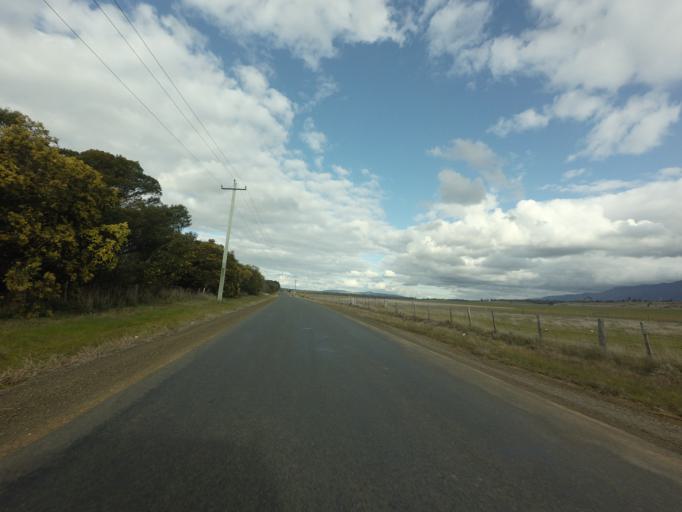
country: AU
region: Tasmania
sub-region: Northern Midlands
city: Longford
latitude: -41.8167
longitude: 147.1957
